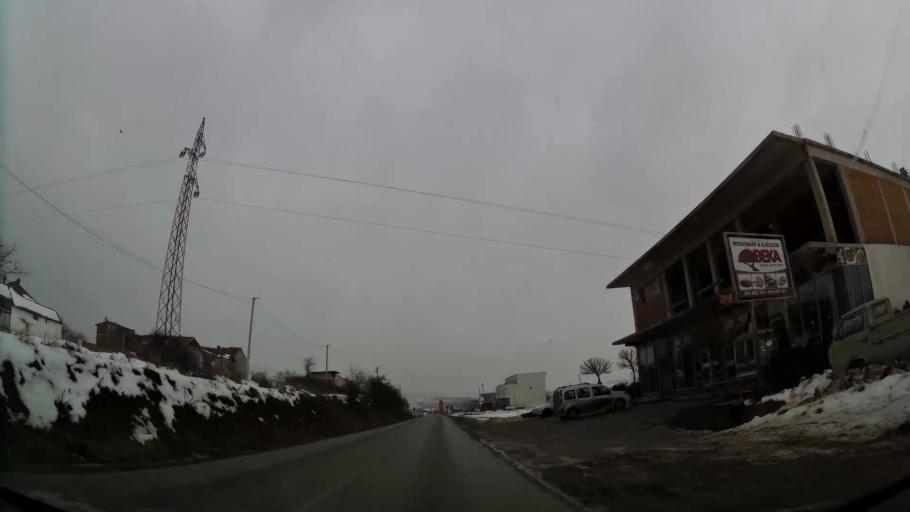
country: XK
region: Pristina
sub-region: Komuna e Prishtines
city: Pristina
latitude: 42.7149
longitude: 21.1501
